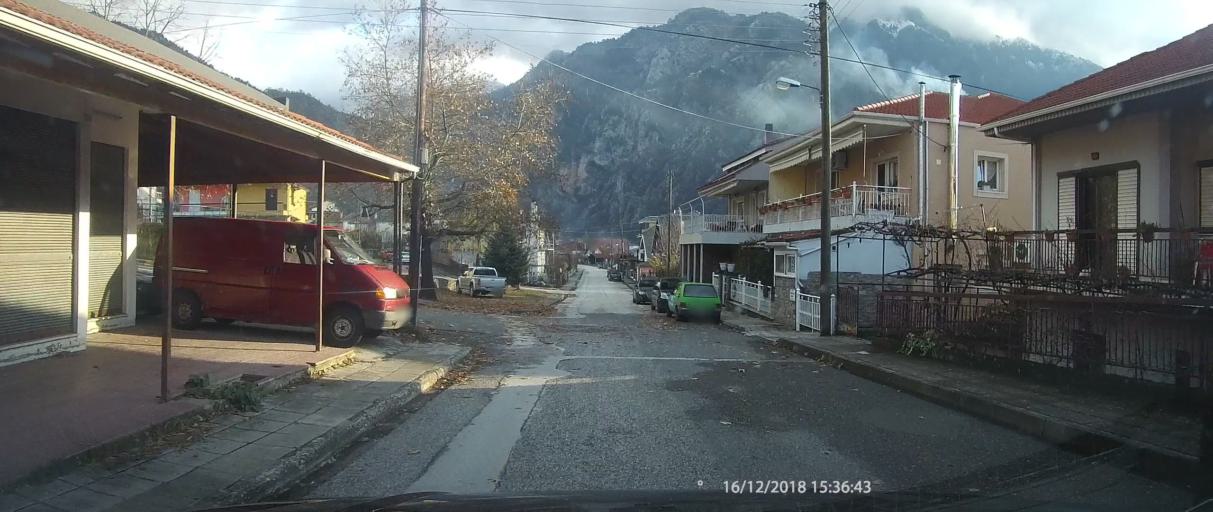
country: GR
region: Epirus
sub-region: Nomos Ioanninon
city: Konitsa
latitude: 40.0455
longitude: 20.7405
